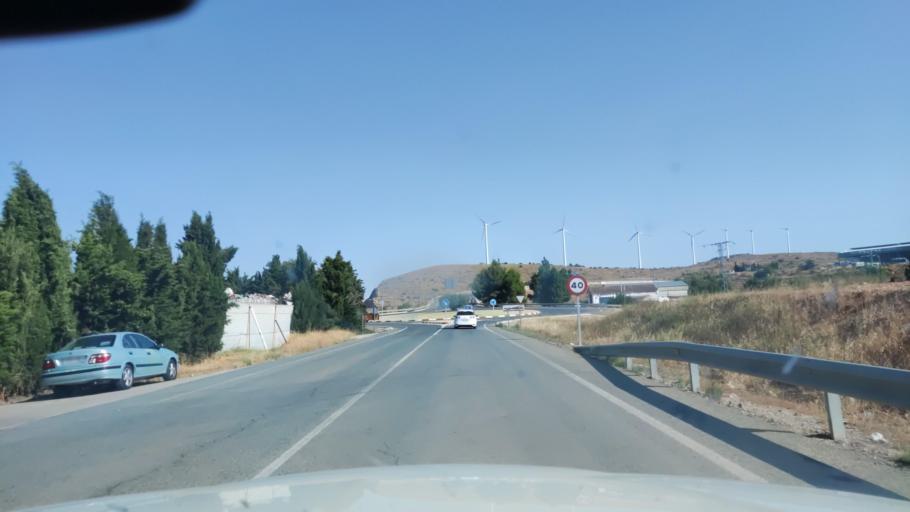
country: ES
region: Castille-La Mancha
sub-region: Provincia de Albacete
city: Pozo-Canada
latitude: 38.7960
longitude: -1.7270
